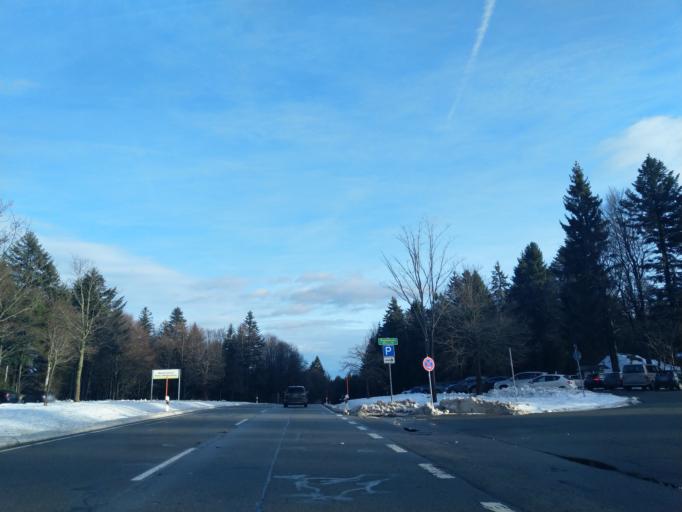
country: DE
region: Bavaria
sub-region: Lower Bavaria
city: Schaufling
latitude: 48.8759
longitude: 13.0652
